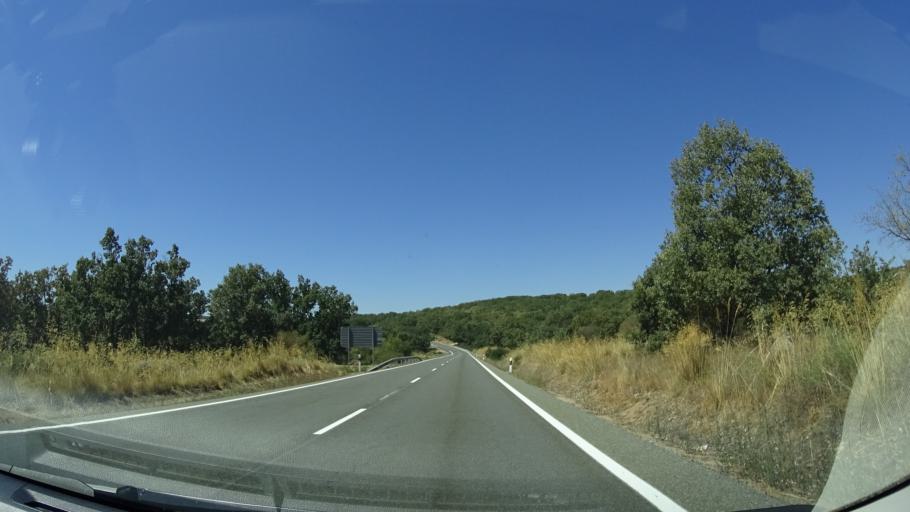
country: ES
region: Castille and Leon
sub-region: Provincia de Avila
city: Navalperal de Pinares
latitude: 40.5912
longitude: -4.4669
